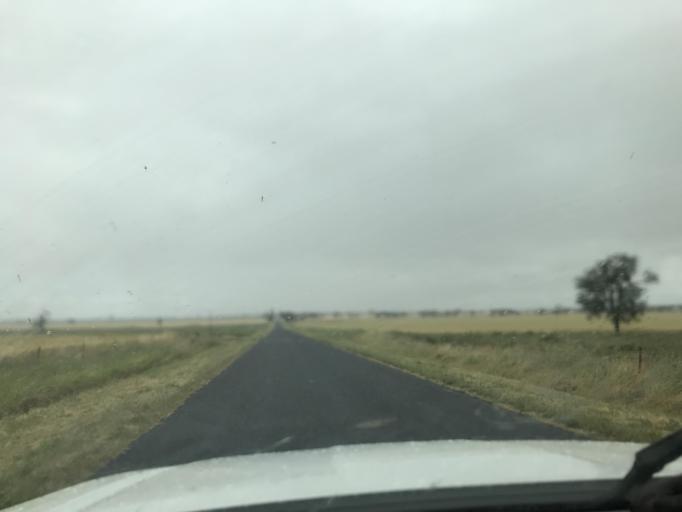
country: AU
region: South Australia
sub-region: Tatiara
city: Bordertown
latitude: -36.3280
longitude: 141.1412
